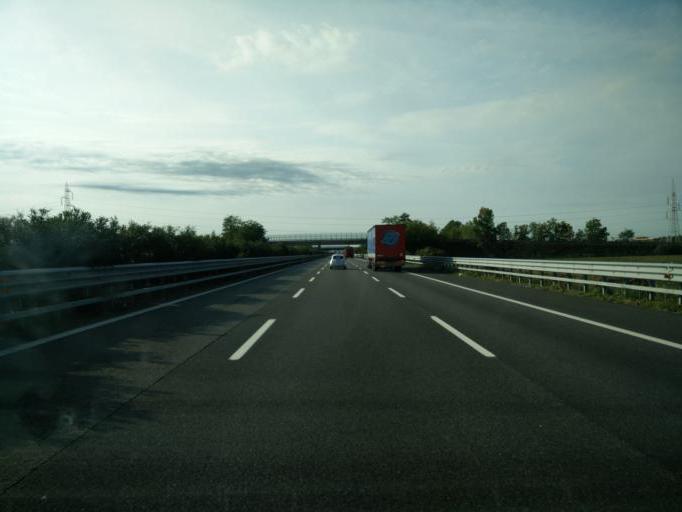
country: IT
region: Lombardy
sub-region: Provincia di Brescia
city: San Zeno Naviglio
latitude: 45.4879
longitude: 10.2263
